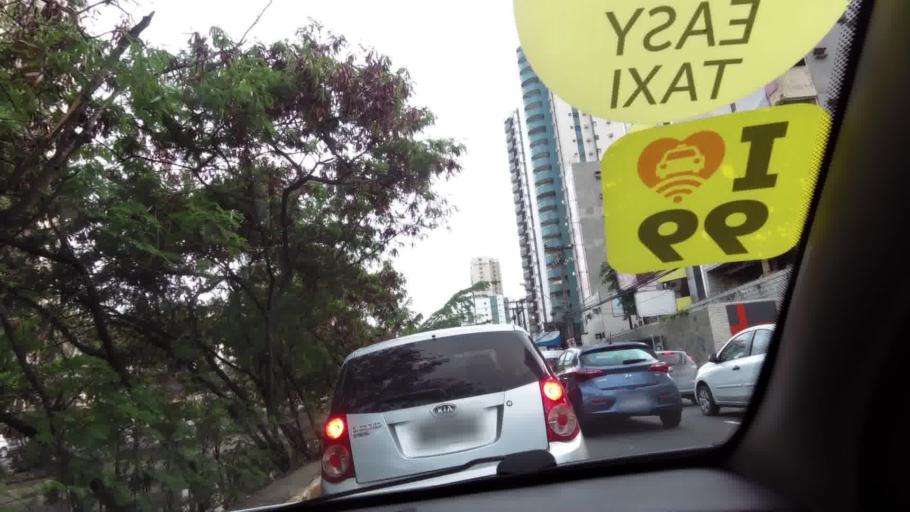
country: BR
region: Pernambuco
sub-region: Recife
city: Recife
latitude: -8.1236
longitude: -34.9016
